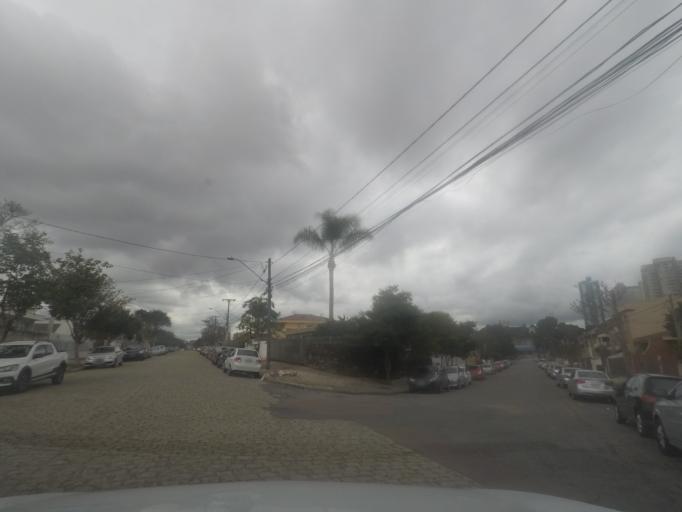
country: BR
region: Parana
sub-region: Curitiba
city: Curitiba
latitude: -25.4408
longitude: -49.2412
